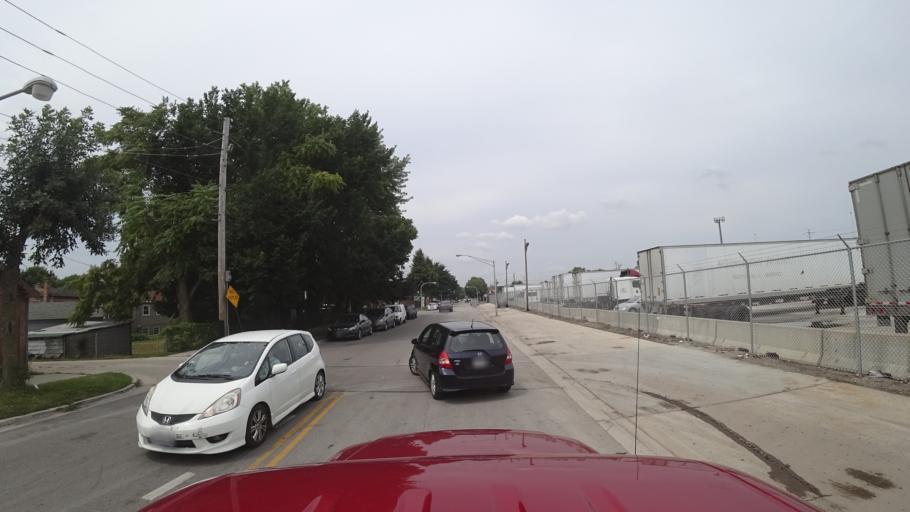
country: US
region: Illinois
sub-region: Cook County
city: Chicago
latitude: 41.8340
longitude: -87.6758
